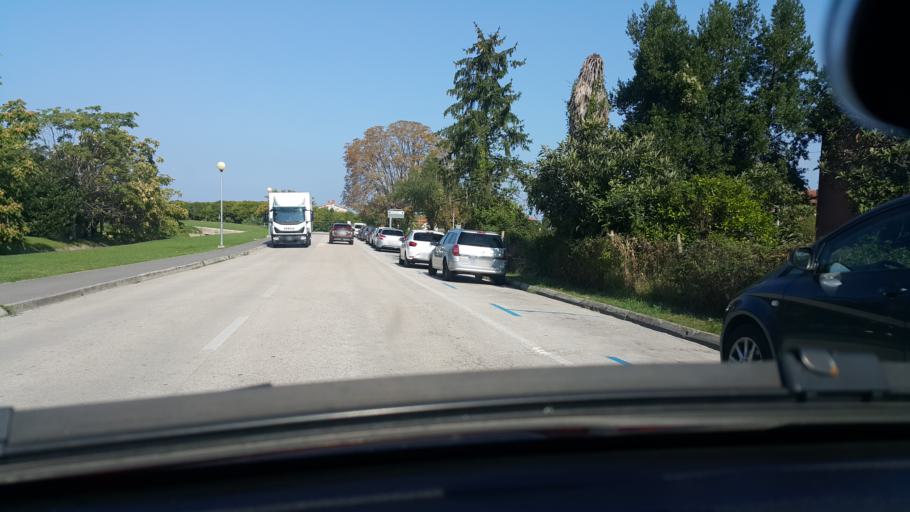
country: SI
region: Izola-Isola
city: Jagodje
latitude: 45.5313
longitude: 13.6494
